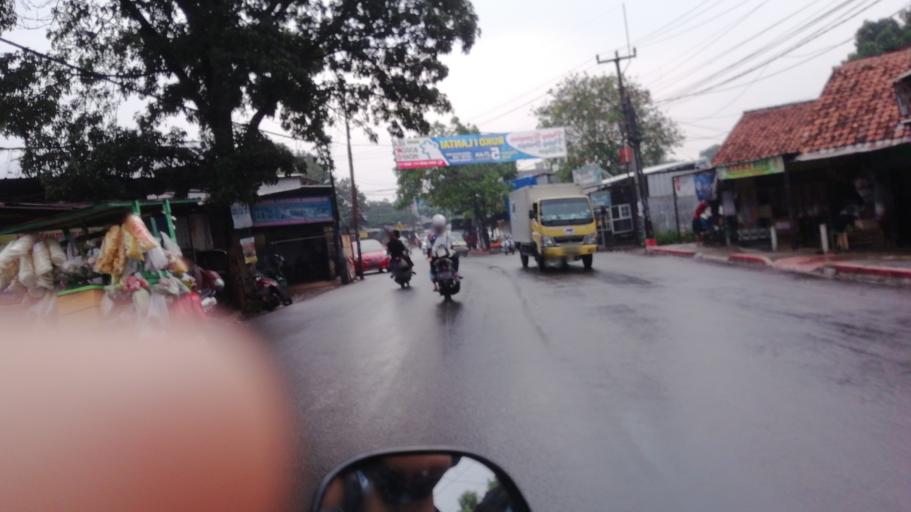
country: ID
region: West Java
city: Bogor
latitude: -6.5313
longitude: 106.8095
